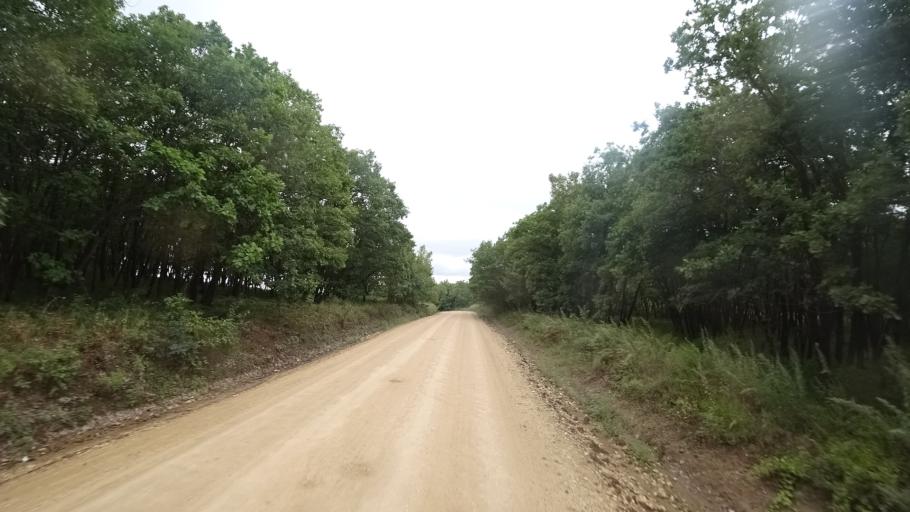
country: RU
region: Primorskiy
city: Chernigovka
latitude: 44.3427
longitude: 132.6181
